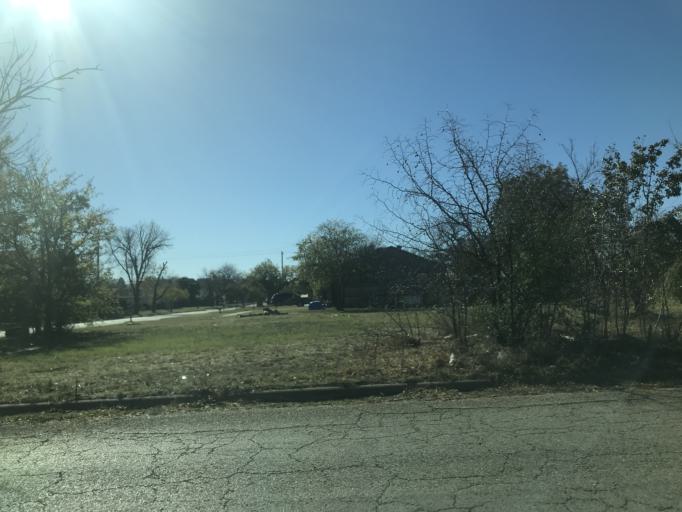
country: US
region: Texas
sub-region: Taylor County
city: Abilene
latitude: 32.4641
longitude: -99.7379
